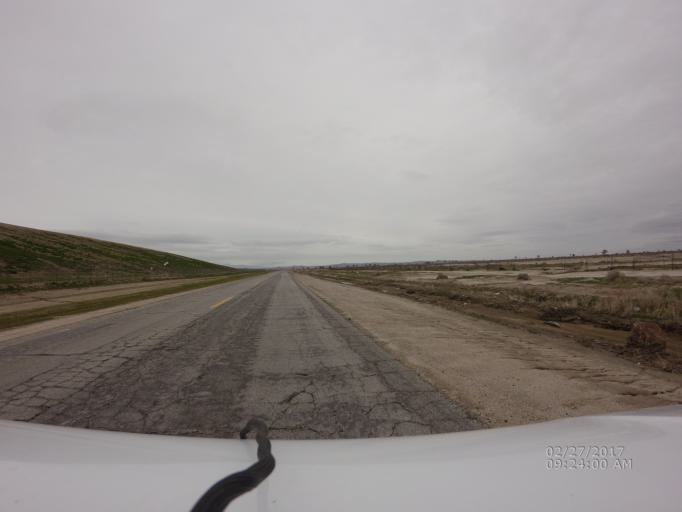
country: US
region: California
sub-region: Los Angeles County
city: Lancaster
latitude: 34.7455
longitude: -118.1131
